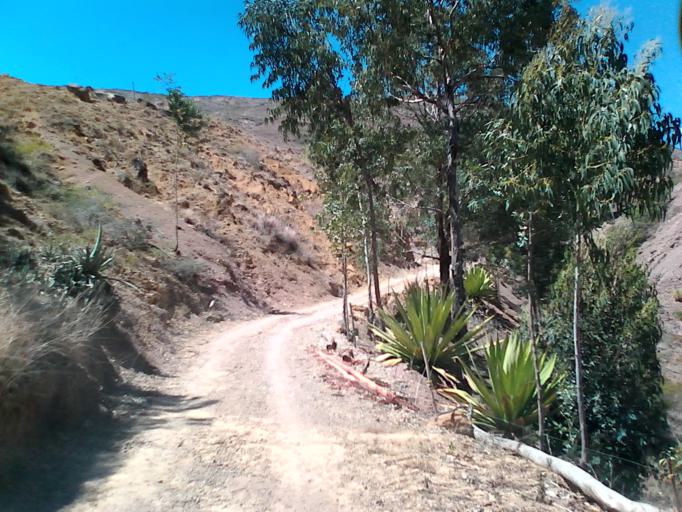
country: CO
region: Boyaca
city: Sachica
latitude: 5.5973
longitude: -73.5717
